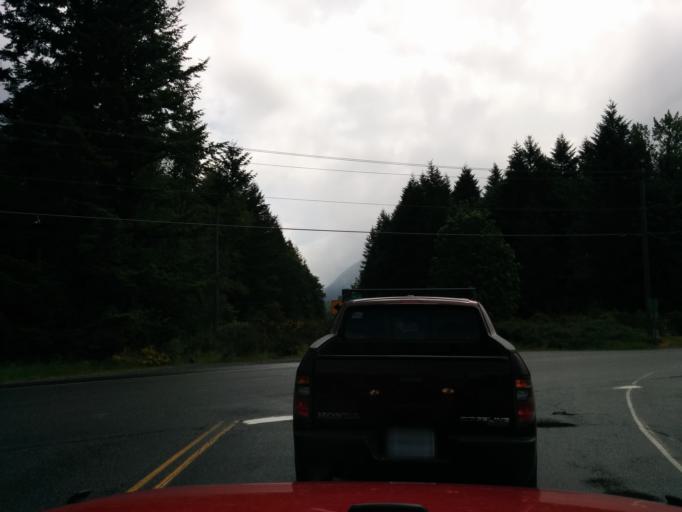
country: US
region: Washington
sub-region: King County
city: Tanner
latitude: 47.4794
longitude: -121.7586
